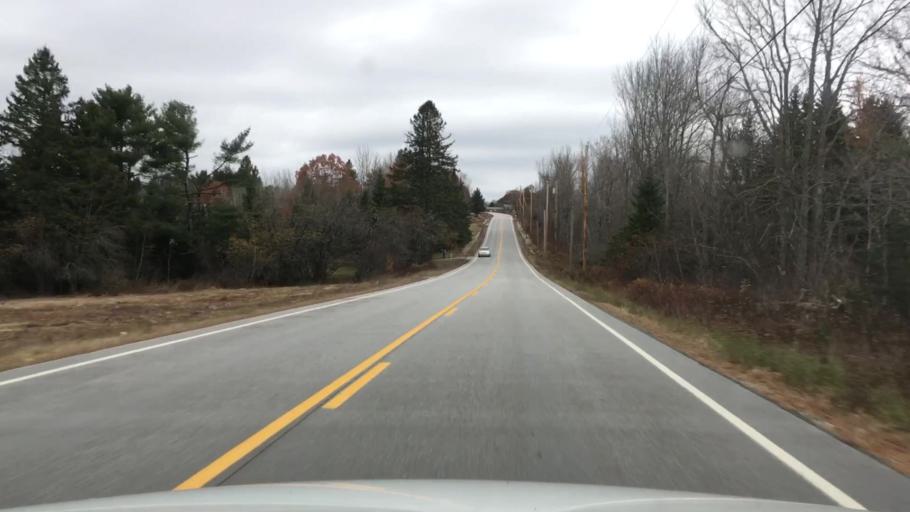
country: US
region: Maine
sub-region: Hancock County
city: Penobscot
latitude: 44.5156
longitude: -68.6581
